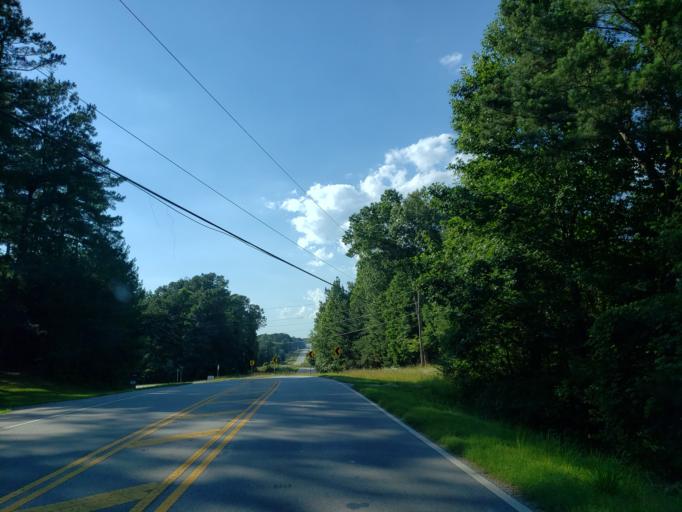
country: US
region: Georgia
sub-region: Haralson County
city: Bremen
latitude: 33.7515
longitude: -85.1579
